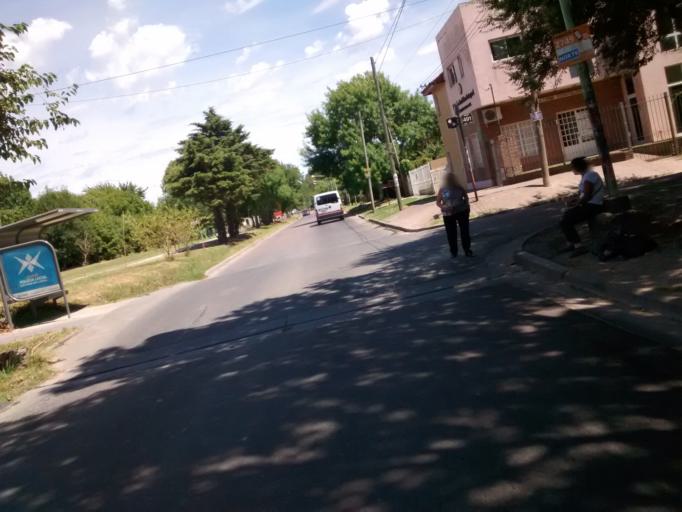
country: AR
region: Buenos Aires
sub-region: Partido de La Plata
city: La Plata
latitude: -34.8753
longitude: -58.0199
